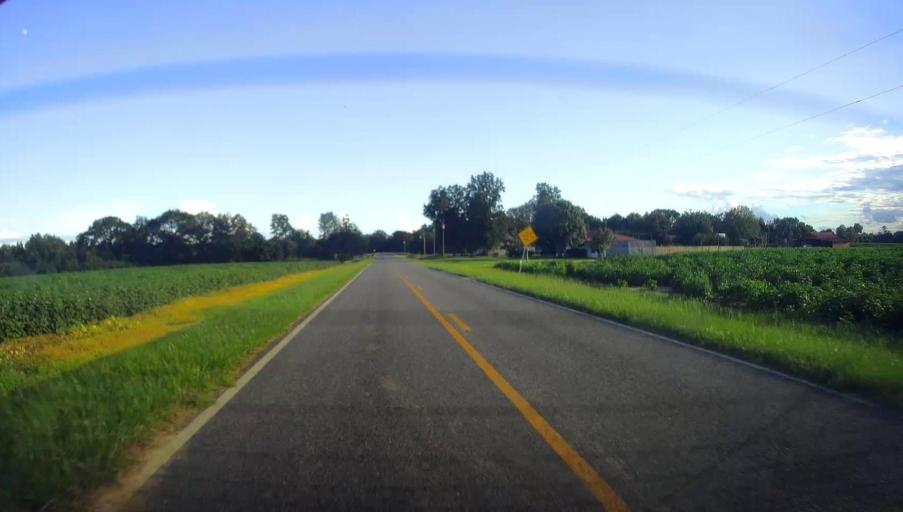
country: US
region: Georgia
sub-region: Pulaski County
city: Hawkinsville
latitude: 32.2764
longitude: -83.5385
